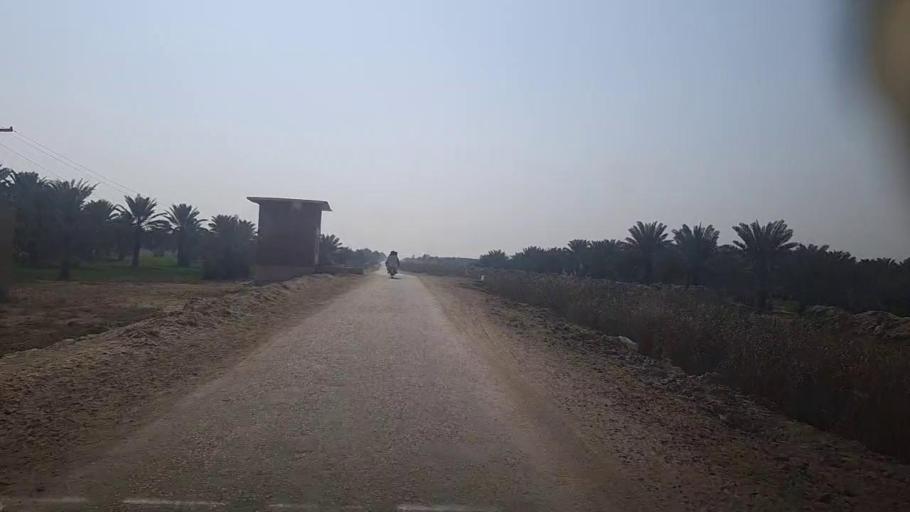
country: PK
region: Sindh
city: Khairpur
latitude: 27.4588
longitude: 68.8155
